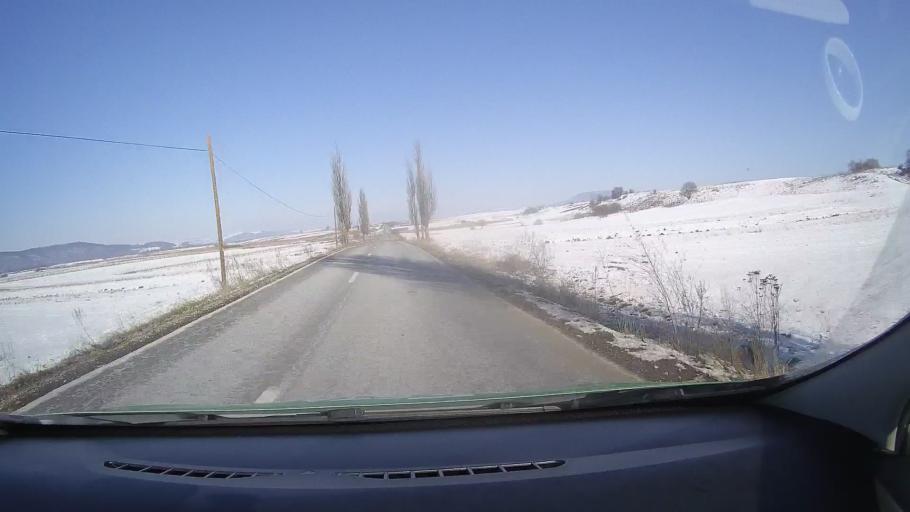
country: RO
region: Brasov
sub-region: Comuna Parau
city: Parau
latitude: 45.8615
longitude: 25.1990
